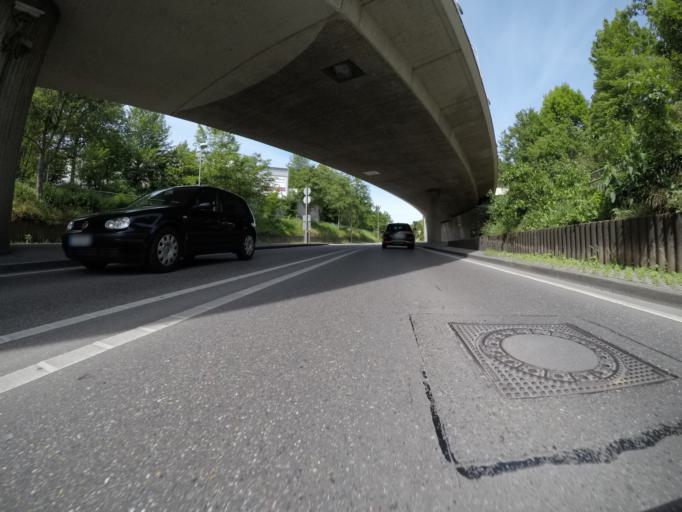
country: DE
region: Baden-Wuerttemberg
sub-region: Regierungsbezirk Stuttgart
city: Stuttgart Feuerbach
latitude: 48.8105
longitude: 9.1413
